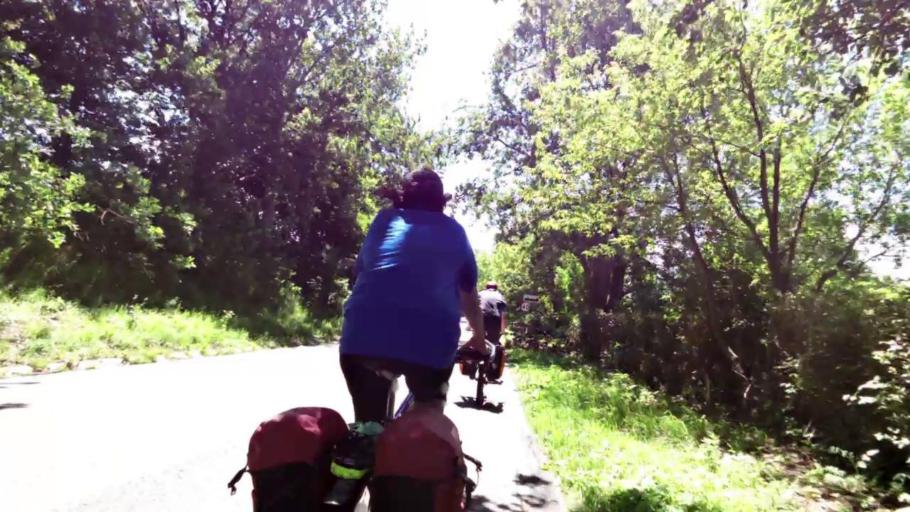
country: PL
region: West Pomeranian Voivodeship
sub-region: Koszalin
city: Koszalin
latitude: 54.2854
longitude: 16.2094
